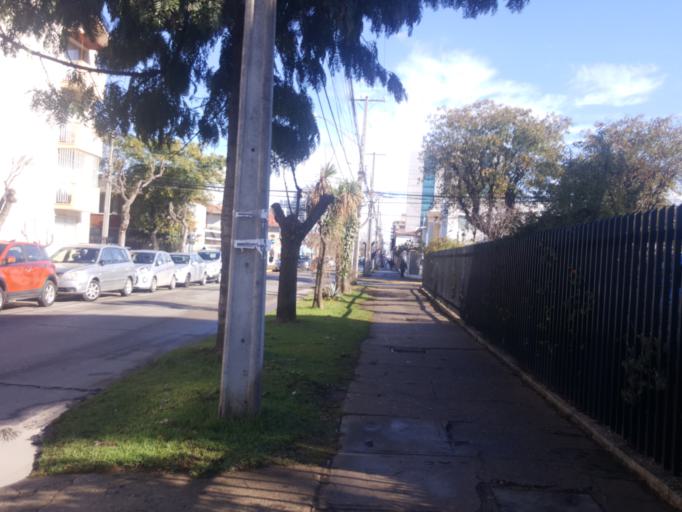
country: CL
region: Valparaiso
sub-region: Provincia de Valparaiso
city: Vina del Mar
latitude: -33.0118
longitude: -71.5448
